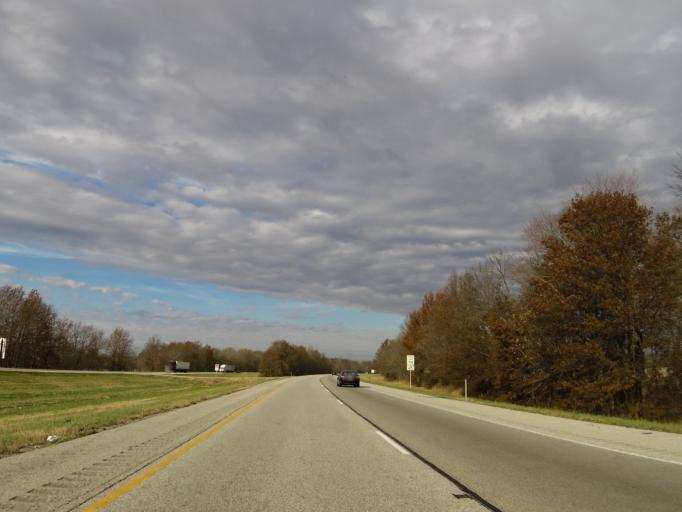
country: US
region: Illinois
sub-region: Washington County
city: Nashville
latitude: 38.3933
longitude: -89.3826
